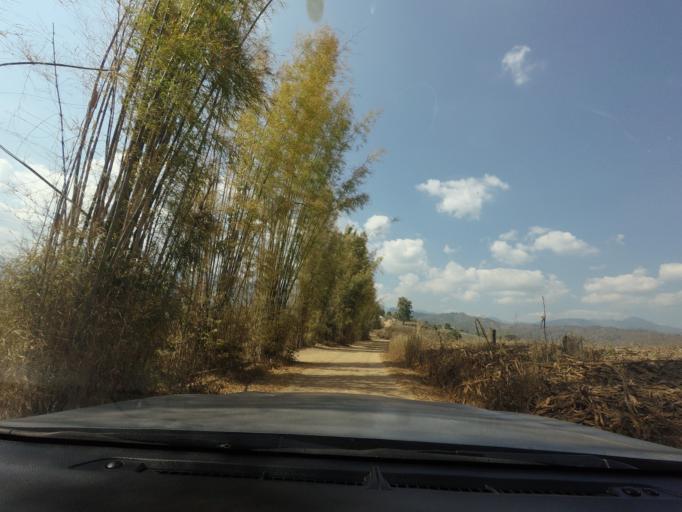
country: TH
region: Mae Hong Son
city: Wiang Nuea
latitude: 19.3997
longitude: 98.4121
